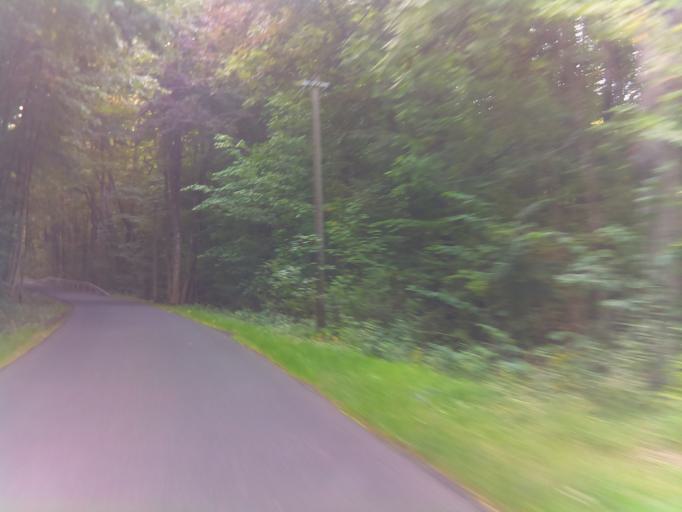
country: DE
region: Bavaria
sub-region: Regierungsbezirk Unterfranken
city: Hausen
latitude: 50.5066
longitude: 10.1187
